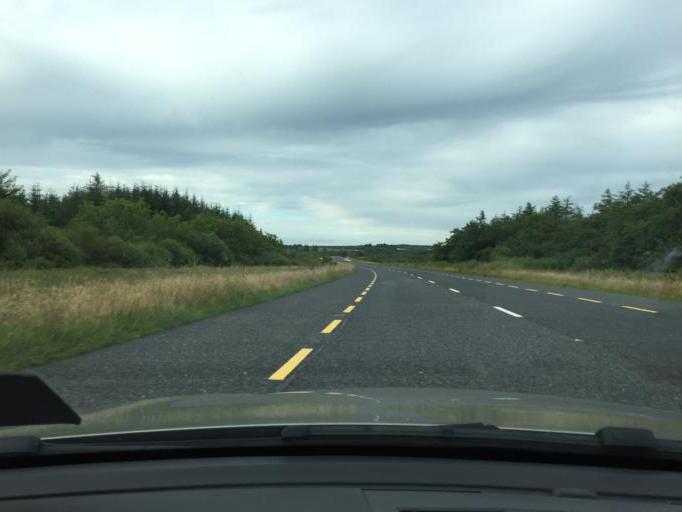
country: IE
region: Munster
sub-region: Waterford
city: Dungarvan
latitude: 52.0302
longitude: -7.6729
